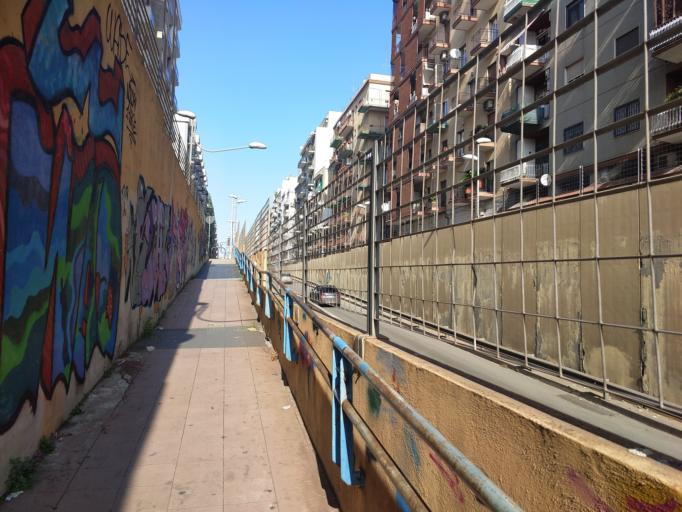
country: IT
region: Apulia
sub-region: Provincia di Bari
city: Bari
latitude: 41.1183
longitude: 16.8524
